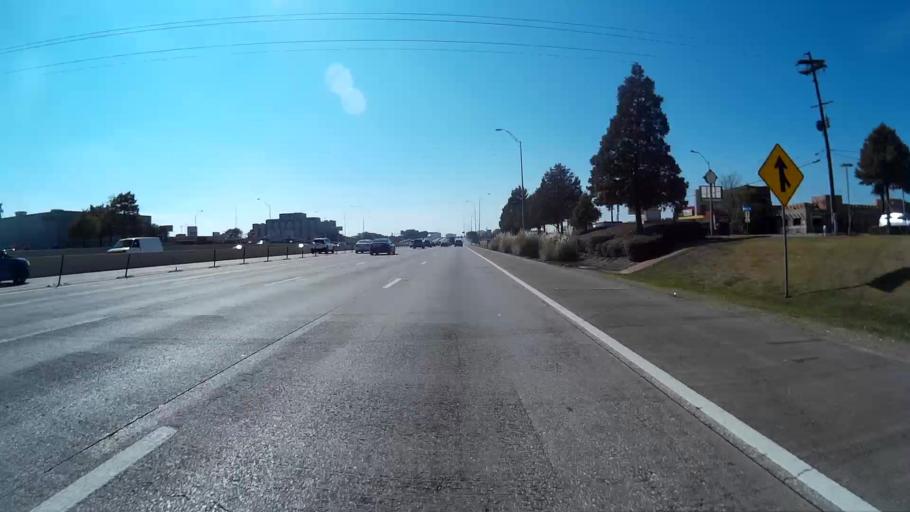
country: US
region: Texas
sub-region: Dallas County
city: Richardson
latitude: 32.9439
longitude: -96.7412
